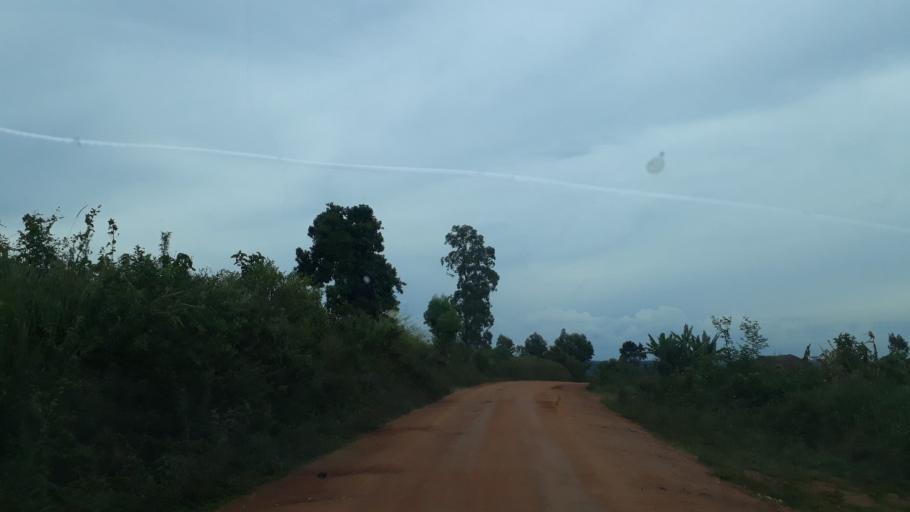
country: UG
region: Northern Region
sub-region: Zombo District
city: Paidha
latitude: 2.0775
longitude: 30.6262
